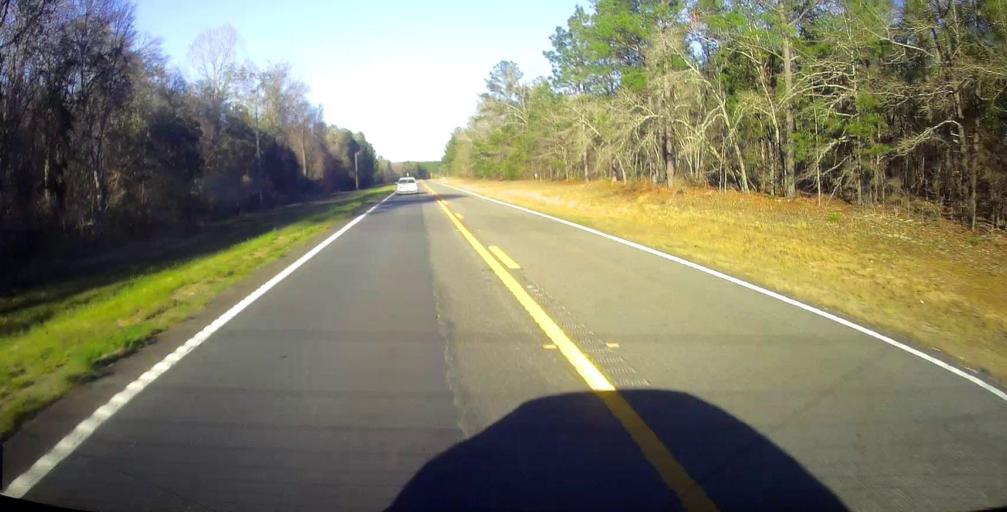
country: US
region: Georgia
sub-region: Taylor County
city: Butler
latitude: 32.5205
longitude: -84.3191
